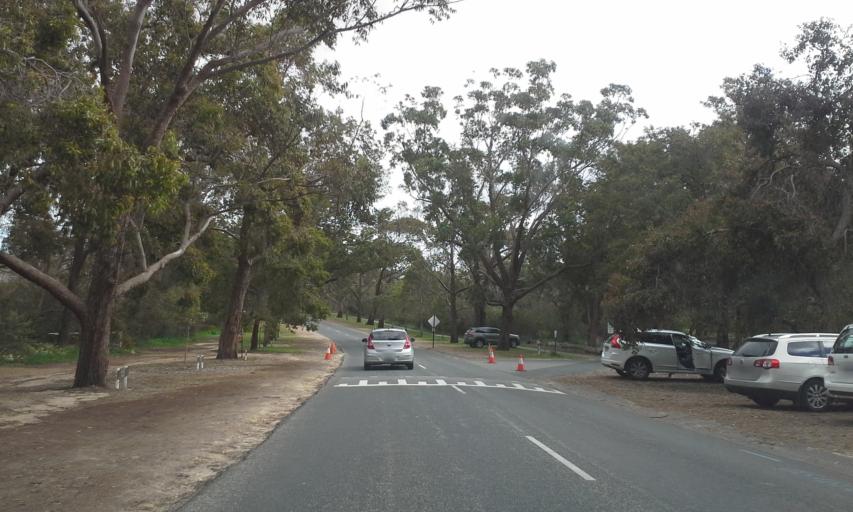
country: AU
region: Western Australia
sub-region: City of Perth
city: West Perth
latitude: -31.9582
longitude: 115.8391
